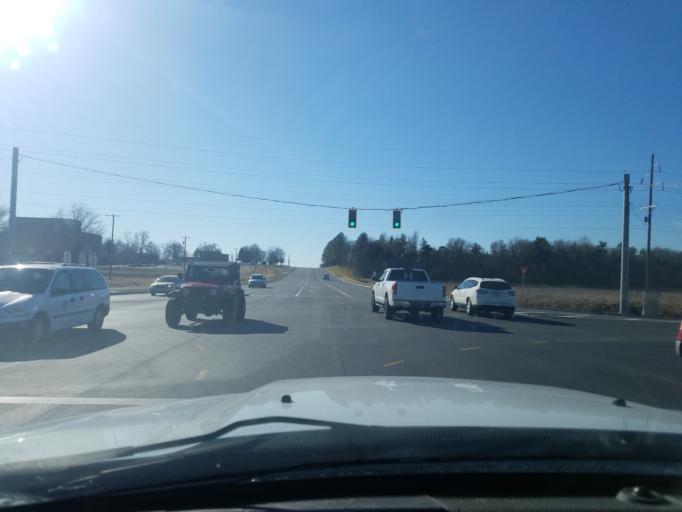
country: US
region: Kentucky
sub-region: Henderson County
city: Henderson
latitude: 37.8000
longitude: -87.6475
